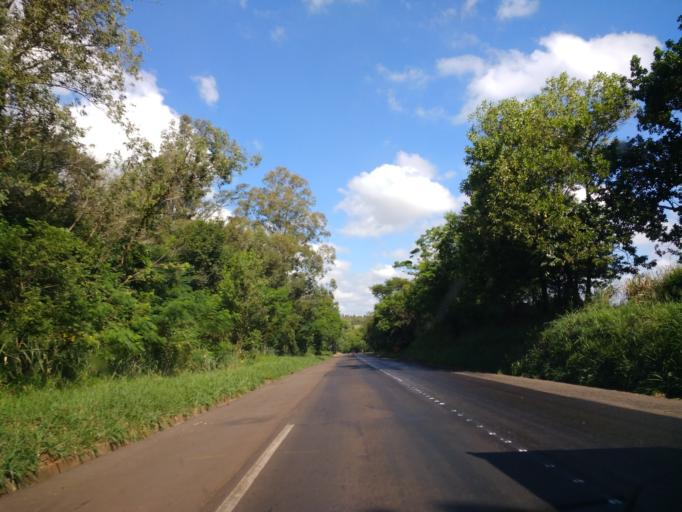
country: BR
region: Parana
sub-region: Umuarama
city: Umuarama
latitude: -23.8756
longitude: -53.3951
